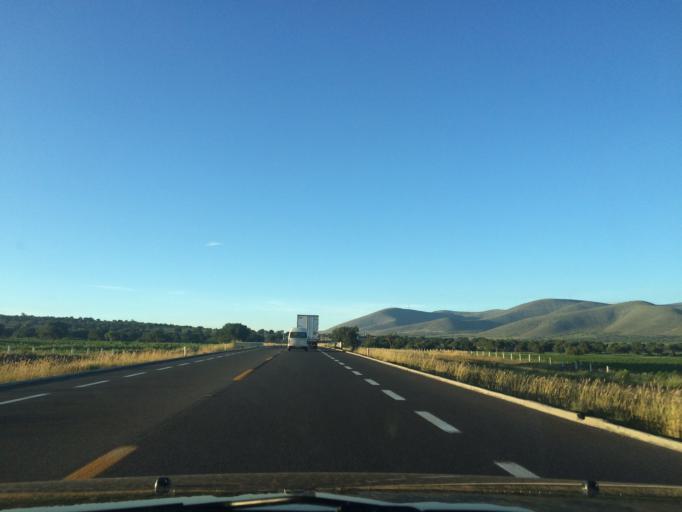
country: MX
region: Puebla
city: Cuacnopalan
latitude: 18.7702
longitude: -97.4849
